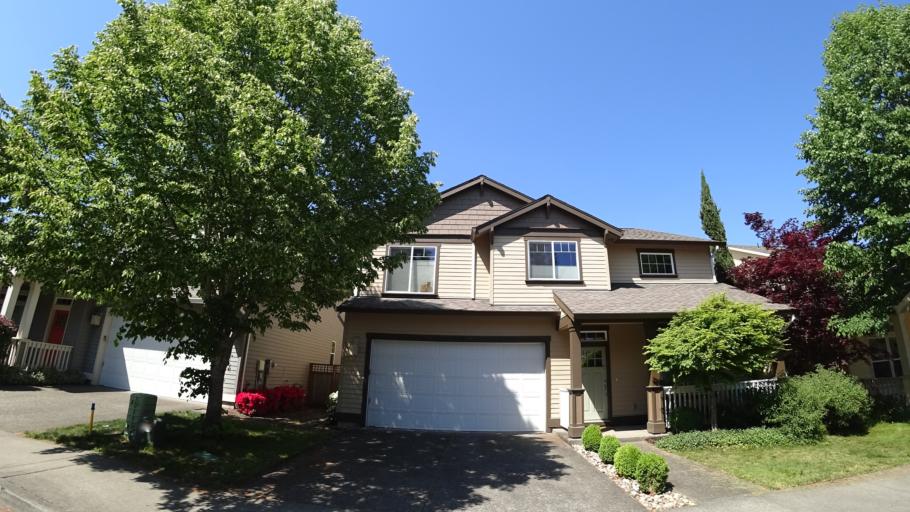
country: US
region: Oregon
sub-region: Washington County
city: Cedar Hills
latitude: 45.4963
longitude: -122.7983
